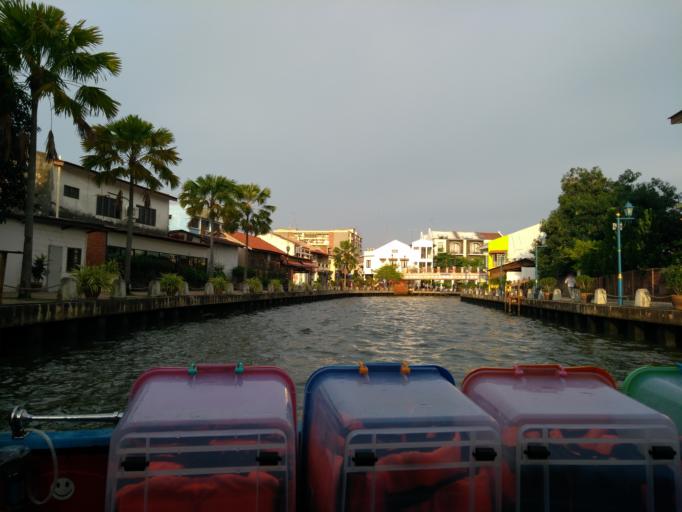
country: MY
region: Melaka
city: Malacca
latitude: 2.1975
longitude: 102.2495
